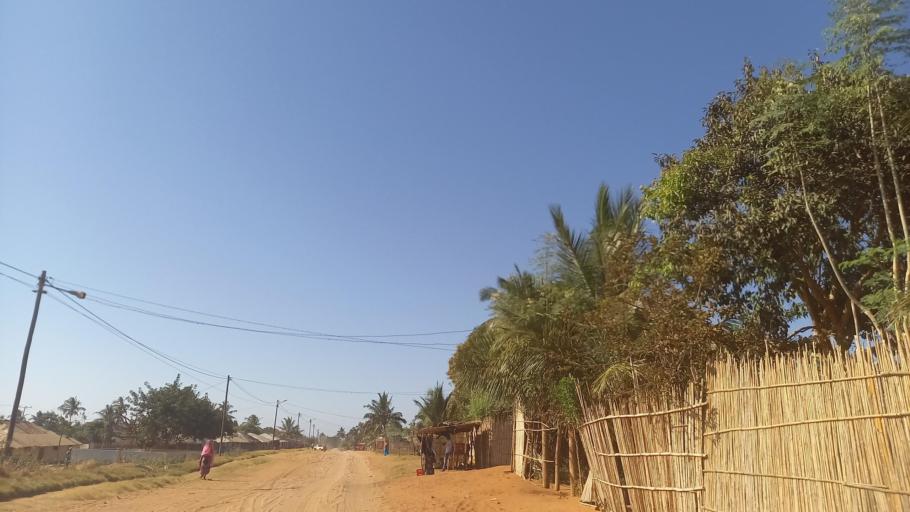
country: MZ
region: Cabo Delgado
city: Pemba
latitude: -13.1386
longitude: 40.5512
